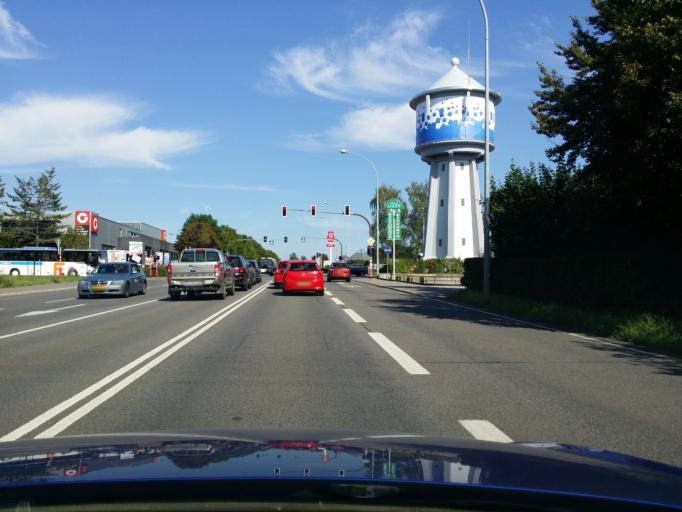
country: LU
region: Luxembourg
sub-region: Canton de Luxembourg
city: Bertrange
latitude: 49.6216
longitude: 6.0466
